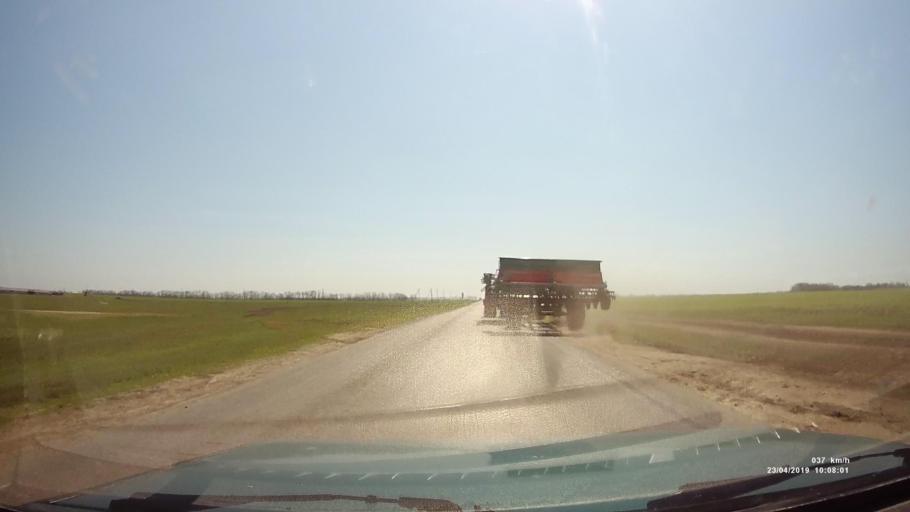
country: RU
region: Rostov
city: Sovetskoye
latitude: 46.7220
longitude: 42.2598
